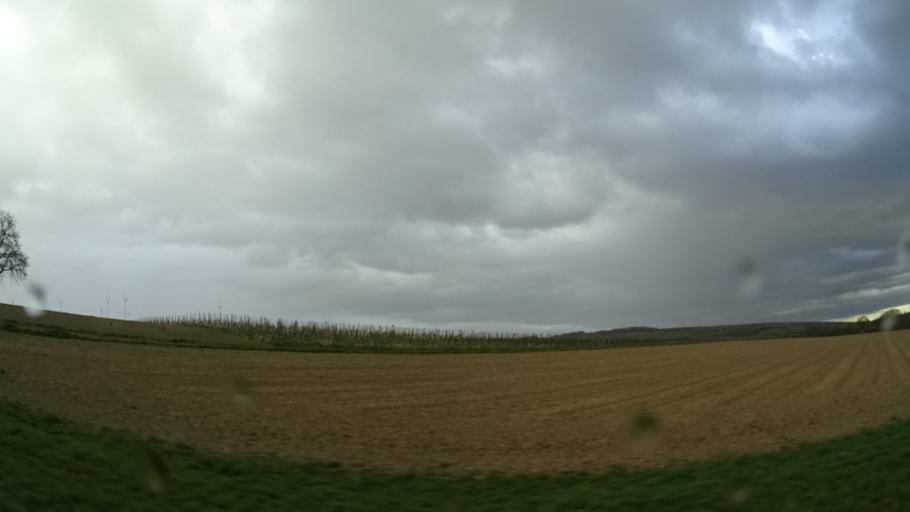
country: DE
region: Rheinland-Pfalz
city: Eppelsheim
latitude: 49.7004
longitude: 8.1726
